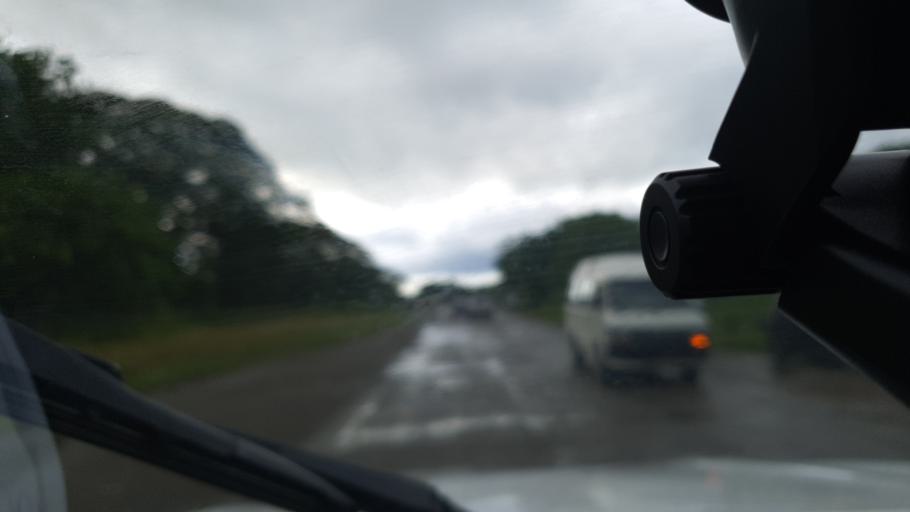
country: SB
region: Guadalcanal
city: Honiara
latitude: -9.4287
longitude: 160.0700
